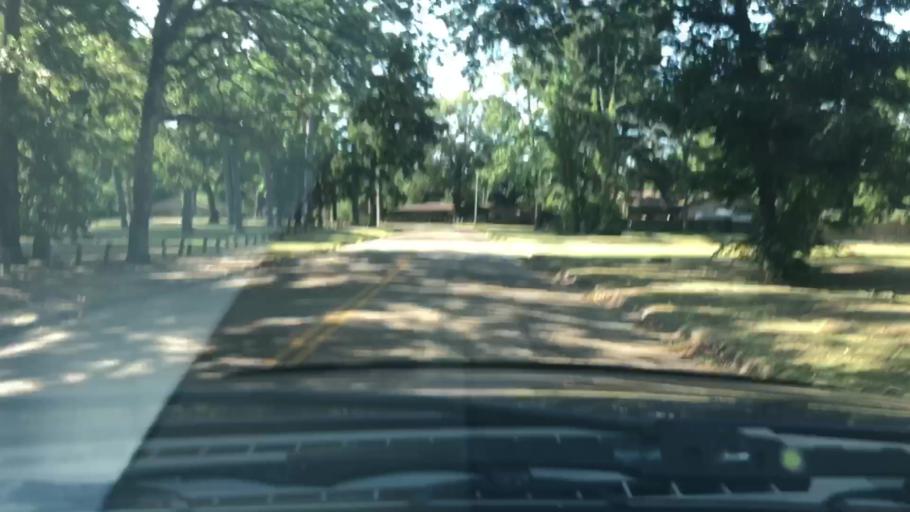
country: US
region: Arkansas
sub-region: Miller County
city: Texarkana
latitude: 33.4602
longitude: -94.0583
